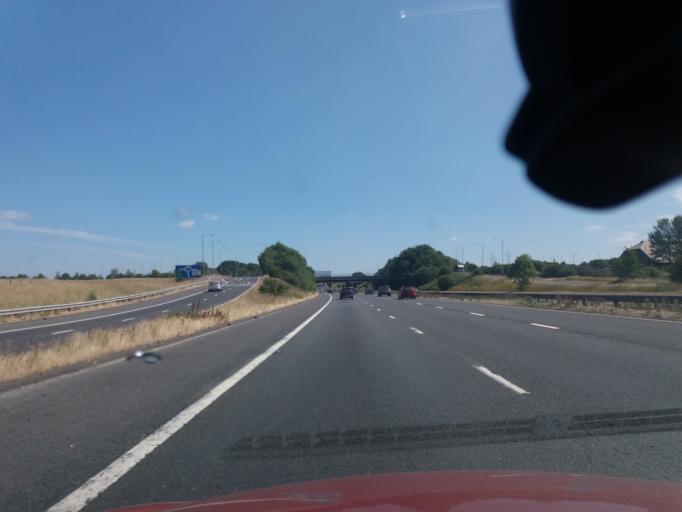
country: GB
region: England
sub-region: Borough of Bolton
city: Horwich
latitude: 53.5768
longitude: -2.5489
